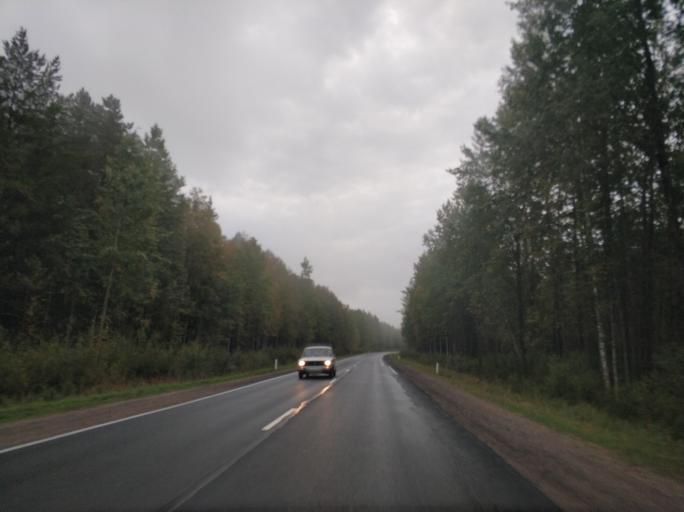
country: RU
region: Leningrad
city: Shcheglovo
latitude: 60.1008
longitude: 30.8307
